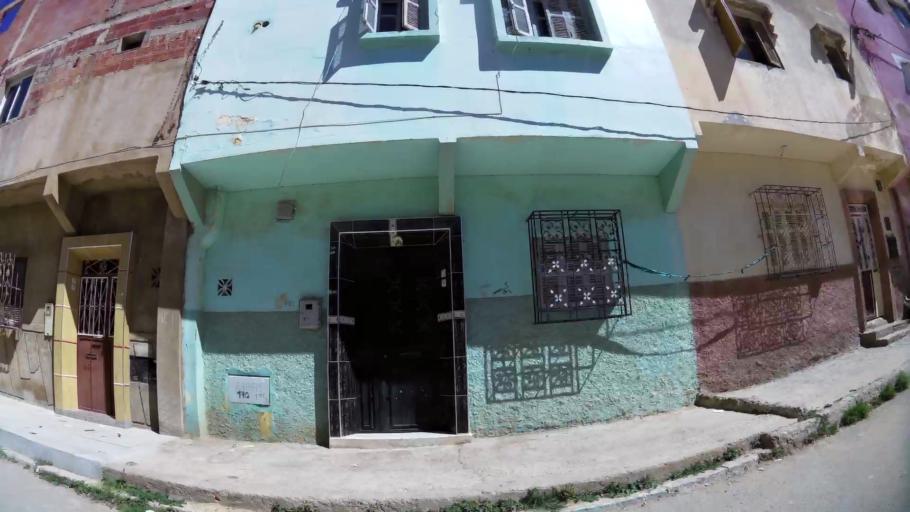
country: MA
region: Meknes-Tafilalet
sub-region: Meknes
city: Meknes
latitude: 33.9110
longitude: -5.5350
